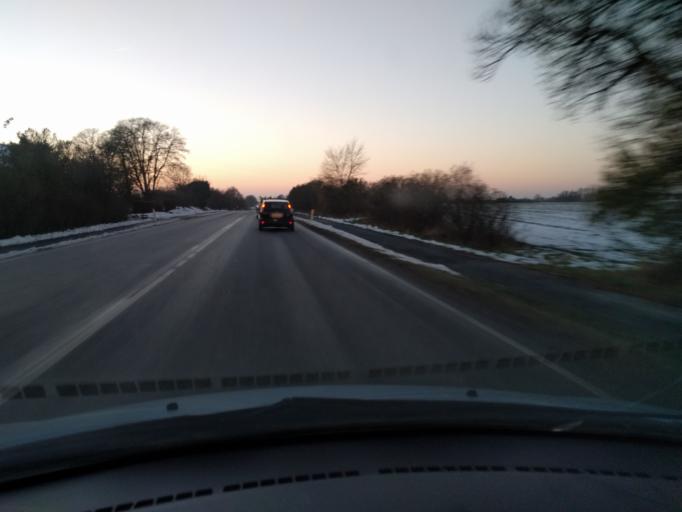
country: DK
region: South Denmark
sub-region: Nyborg Kommune
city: Ullerslev
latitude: 55.3602
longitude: 10.6889
